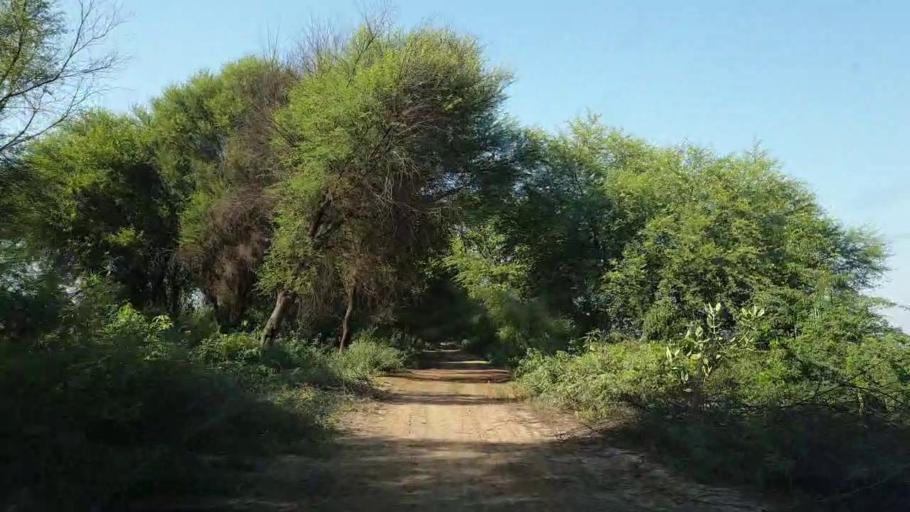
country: PK
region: Sindh
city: Tando Jam
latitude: 25.3567
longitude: 68.5698
